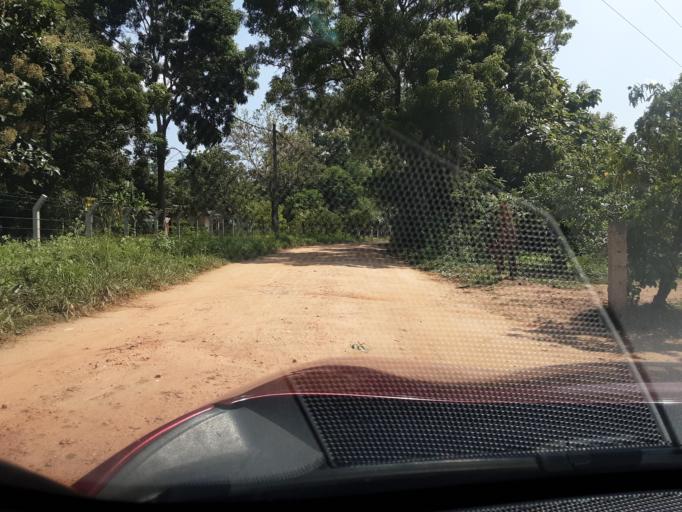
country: LK
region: Central
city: Sigiriya
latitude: 8.0048
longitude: 80.7466
